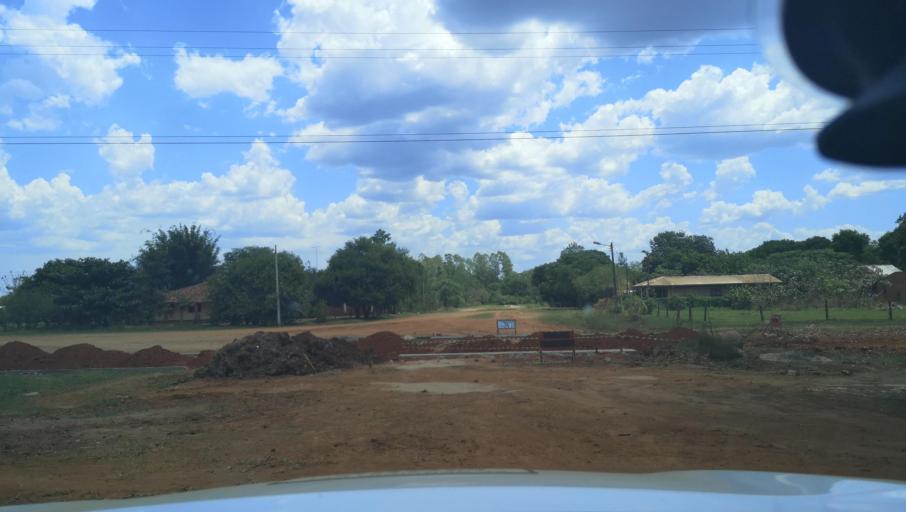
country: PY
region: Itapua
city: Carmen del Parana
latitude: -27.1720
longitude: -56.2393
